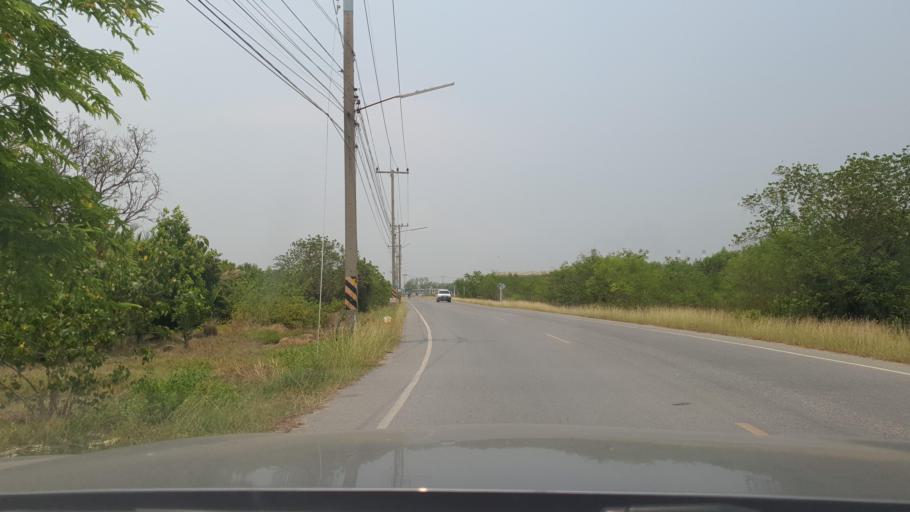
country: TH
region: Chachoengsao
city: Bang Pakong
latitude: 13.4844
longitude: 101.0146
